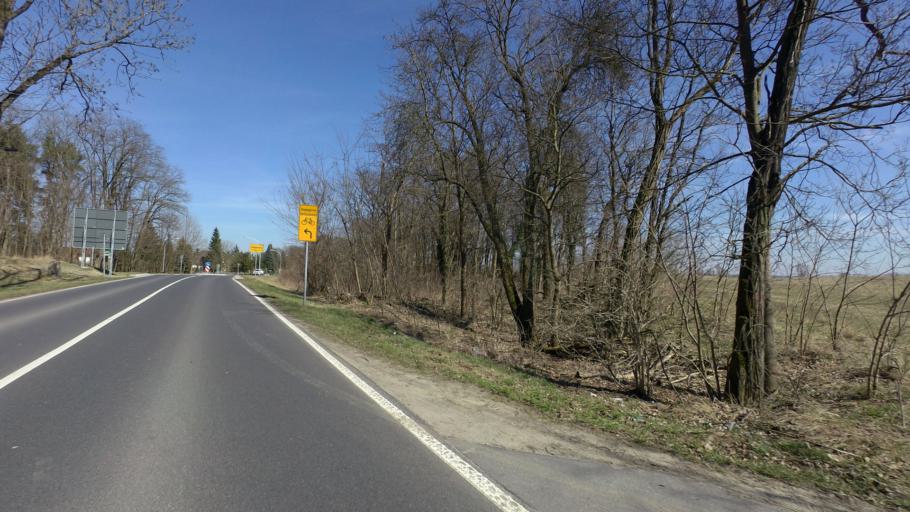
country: DE
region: Brandenburg
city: Muncheberg
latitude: 52.4999
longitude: 14.1085
